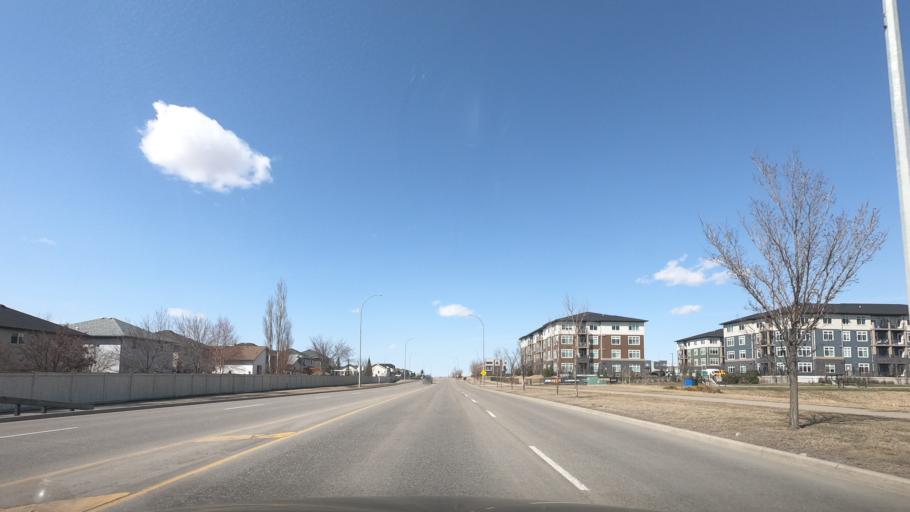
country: CA
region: Alberta
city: Airdrie
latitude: 51.3034
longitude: -114.0133
